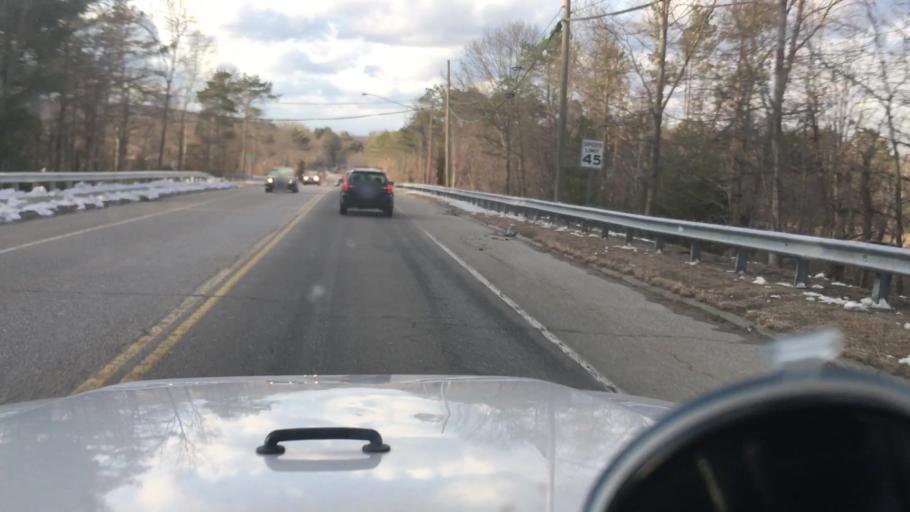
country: US
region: Connecticut
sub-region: New London County
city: Central Waterford
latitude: 41.3361
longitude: -72.1363
